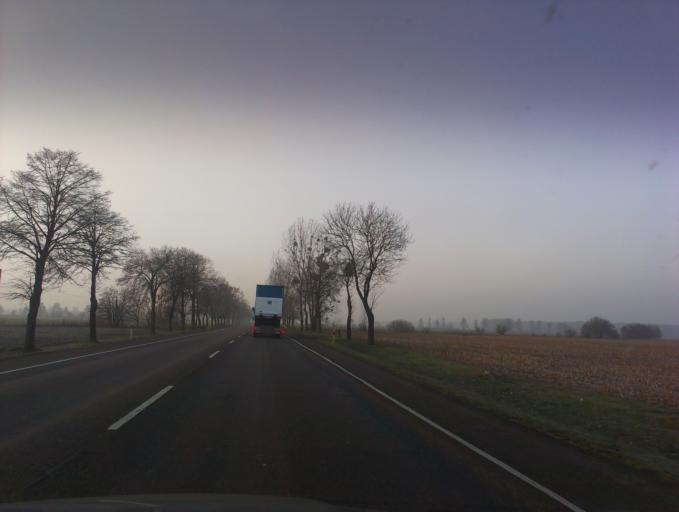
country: PL
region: Greater Poland Voivodeship
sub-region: Powiat obornicki
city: Rogozno
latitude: 52.7545
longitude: 16.9606
